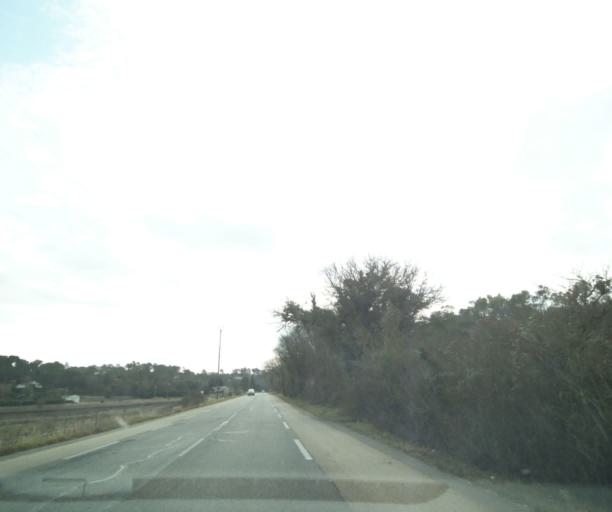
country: FR
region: Provence-Alpes-Cote d'Azur
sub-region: Departement du Var
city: Tourves
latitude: 43.4178
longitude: 5.9123
